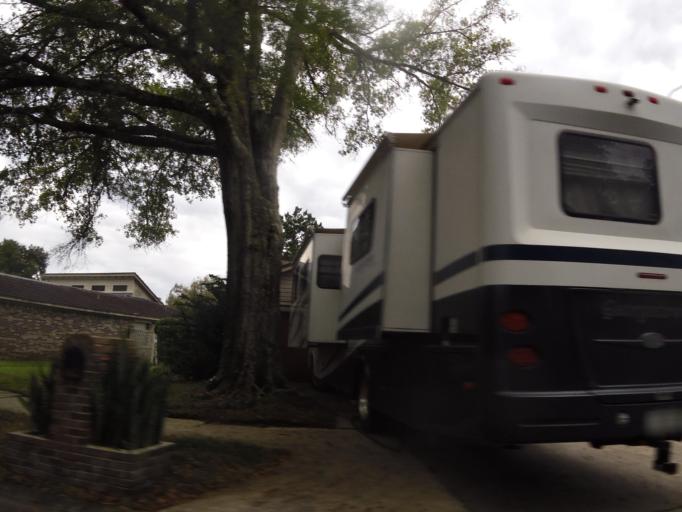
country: US
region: Florida
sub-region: Duval County
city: Jacksonville
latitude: 30.2673
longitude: -81.5984
